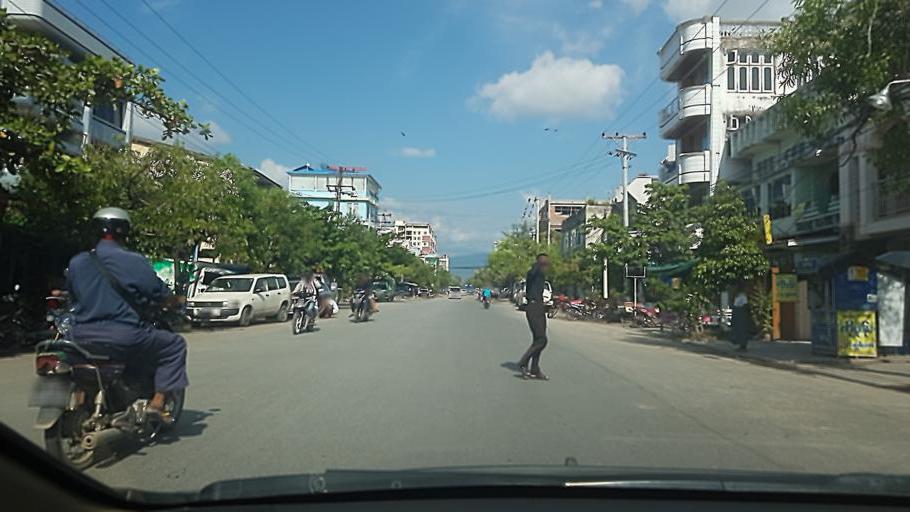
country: MM
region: Mandalay
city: Mandalay
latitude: 21.9814
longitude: 96.0901
